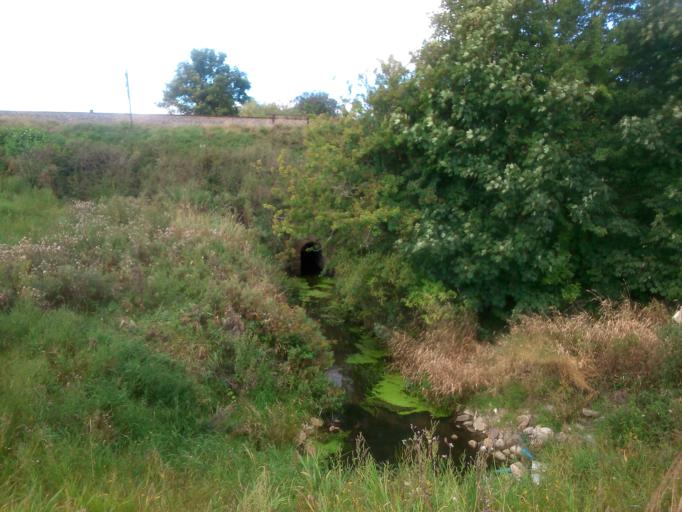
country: DK
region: North Denmark
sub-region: Thisted Kommune
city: Thisted
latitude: 56.9494
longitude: 8.5875
